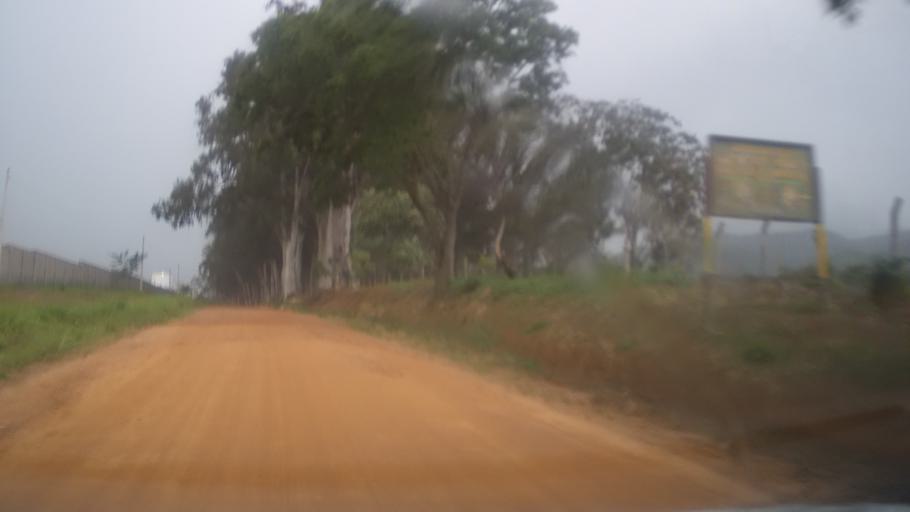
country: BR
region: Sao Paulo
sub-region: Jundiai
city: Jundiai
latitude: -23.2038
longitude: -46.9756
